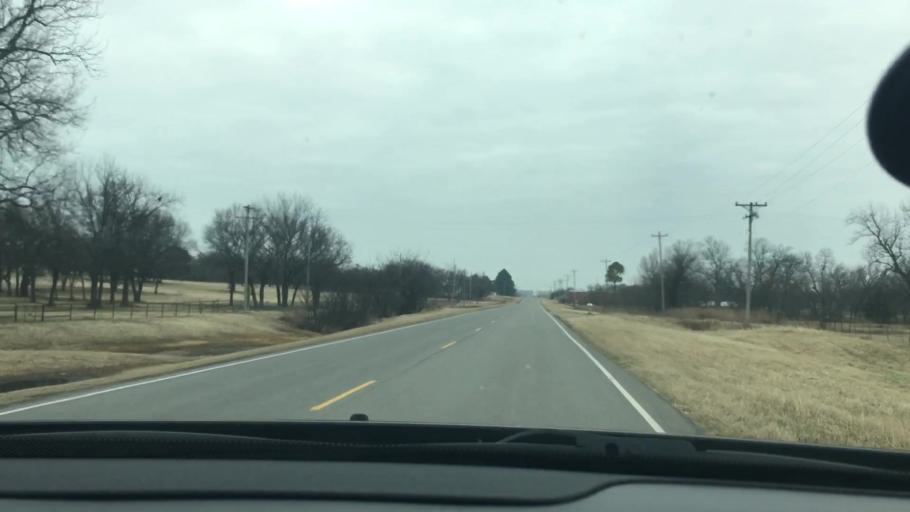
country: US
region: Oklahoma
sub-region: Carter County
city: Healdton
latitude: 34.2571
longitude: -97.4923
